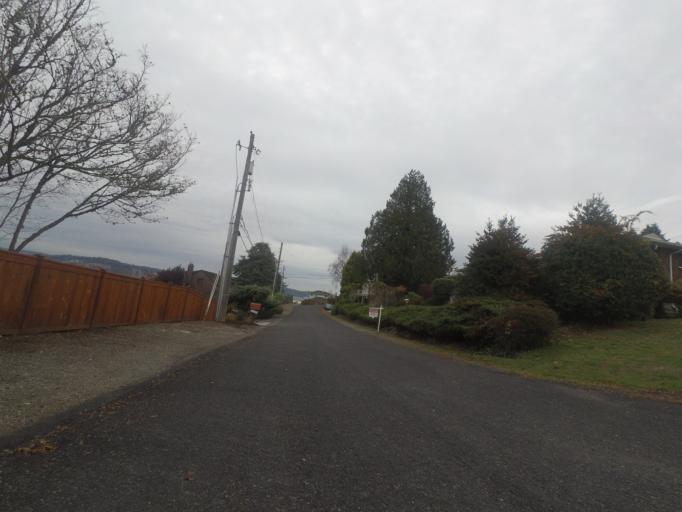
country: US
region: Washington
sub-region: Pierce County
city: University Place
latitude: 47.2323
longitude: -122.5616
